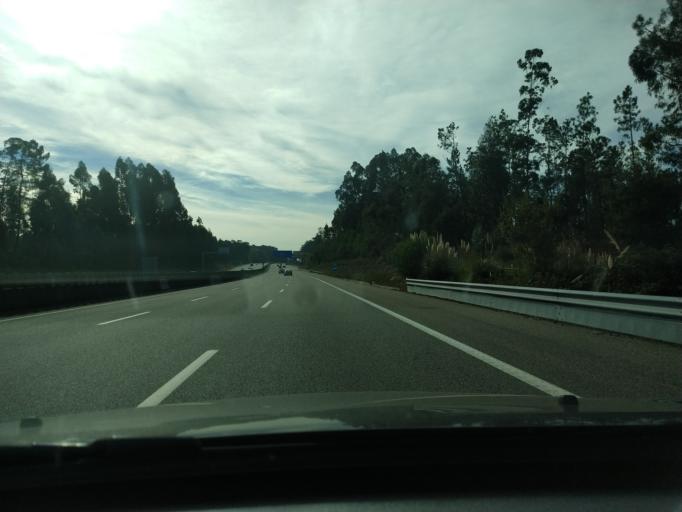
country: PT
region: Aveiro
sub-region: Santa Maria da Feira
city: Rio Meao
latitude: 40.9363
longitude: -8.5730
